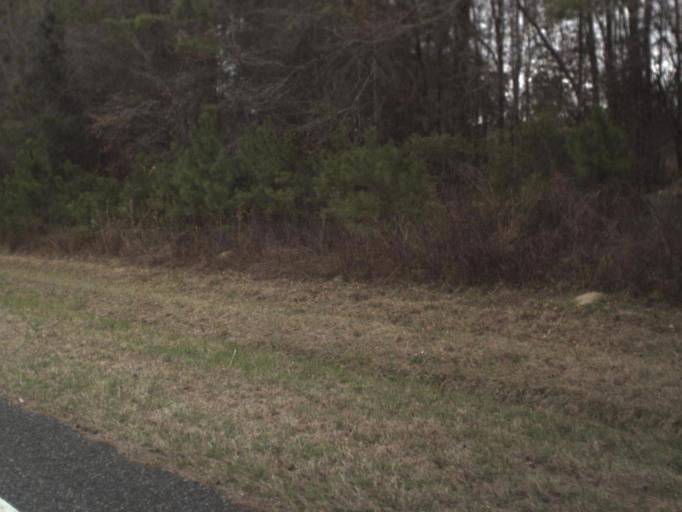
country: US
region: Florida
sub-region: Leon County
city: Woodville
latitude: 30.4024
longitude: -84.0513
